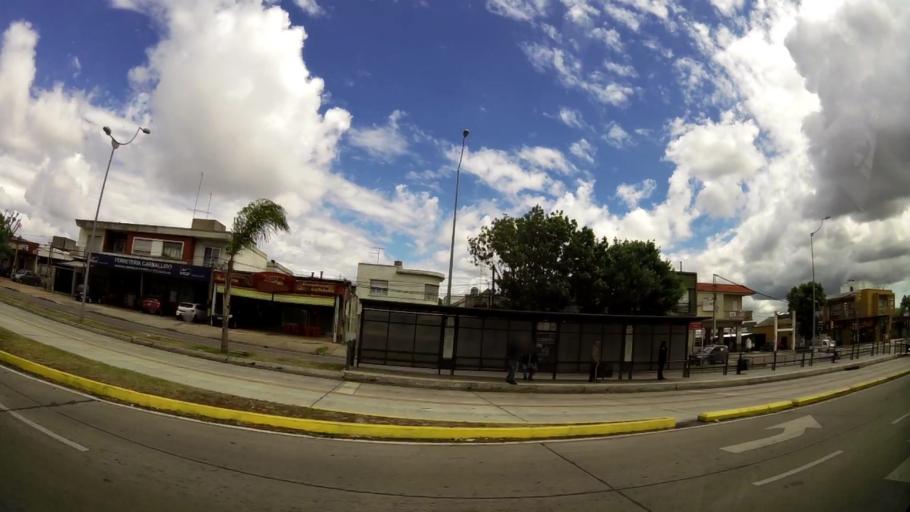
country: UY
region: Montevideo
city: Montevideo
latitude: -34.8469
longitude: -56.1558
